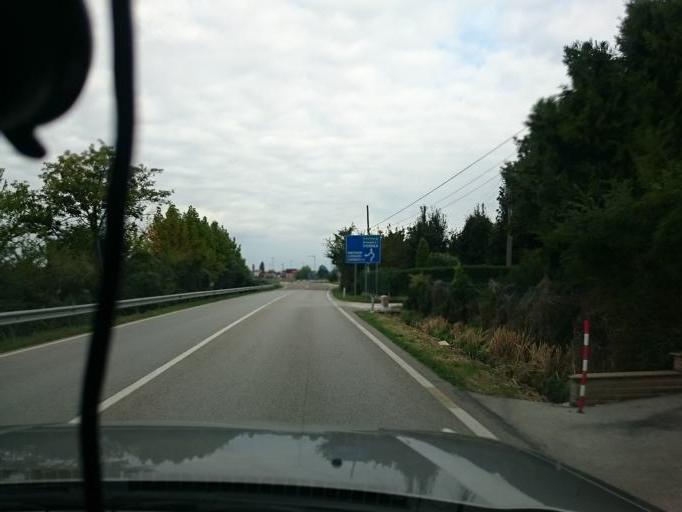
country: IT
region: Veneto
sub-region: Provincia di Padova
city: Arlesega
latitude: 45.4700
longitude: 11.7100
